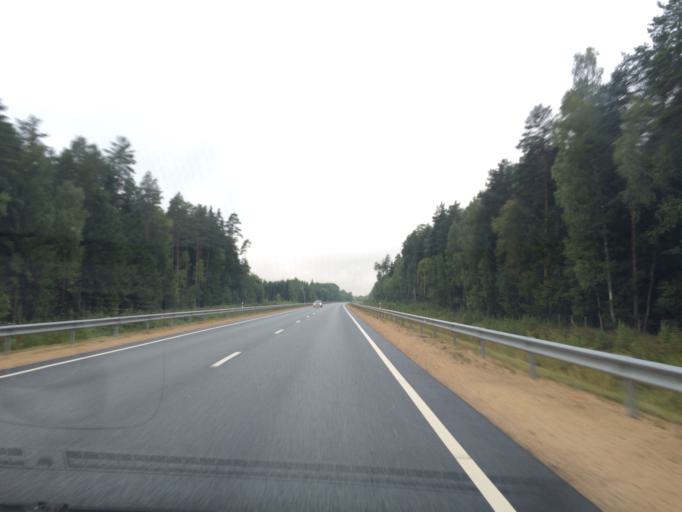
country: LV
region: Lielvarde
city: Lielvarde
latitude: 56.8028
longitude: 24.9113
